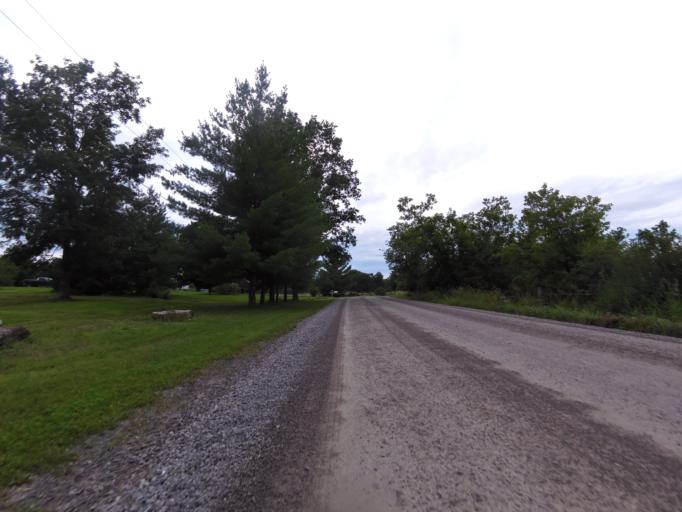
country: CA
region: Ontario
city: Carleton Place
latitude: 45.1451
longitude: -76.1714
